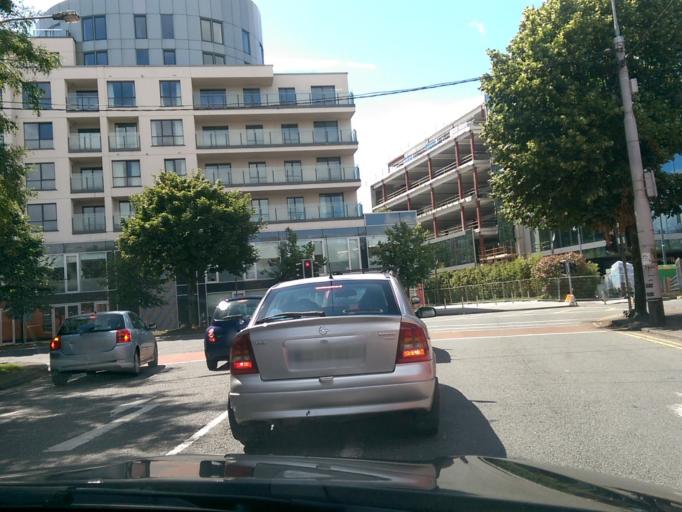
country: IE
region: Munster
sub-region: County Cork
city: Cork
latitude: 51.8973
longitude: -8.4623
